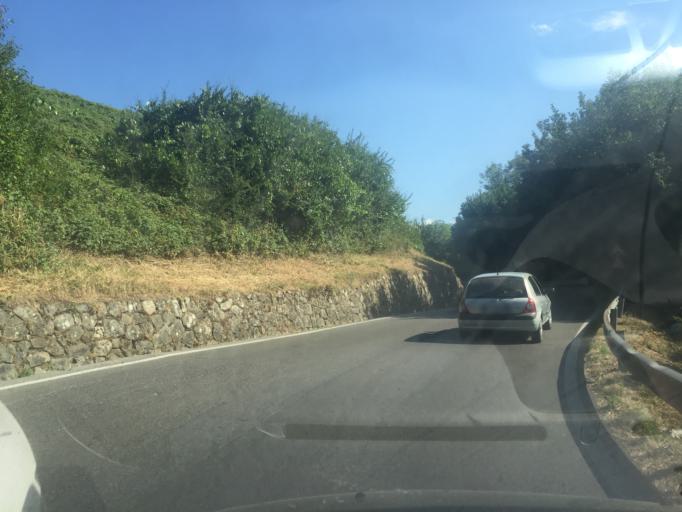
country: IT
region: Tuscany
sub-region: Provincia di Lucca
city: Castelnuovo di Garfagnana
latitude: 44.1230
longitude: 10.3919
